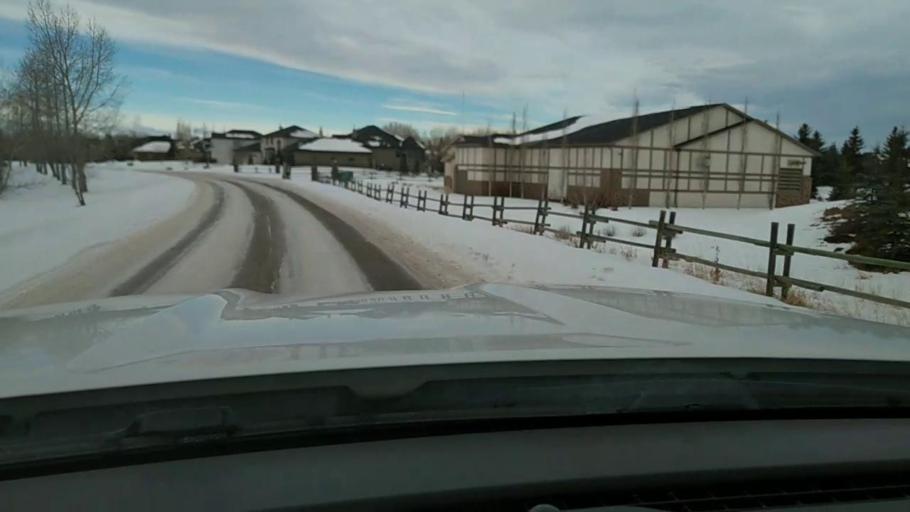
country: CA
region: Alberta
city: Calgary
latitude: 51.1169
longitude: -114.2607
